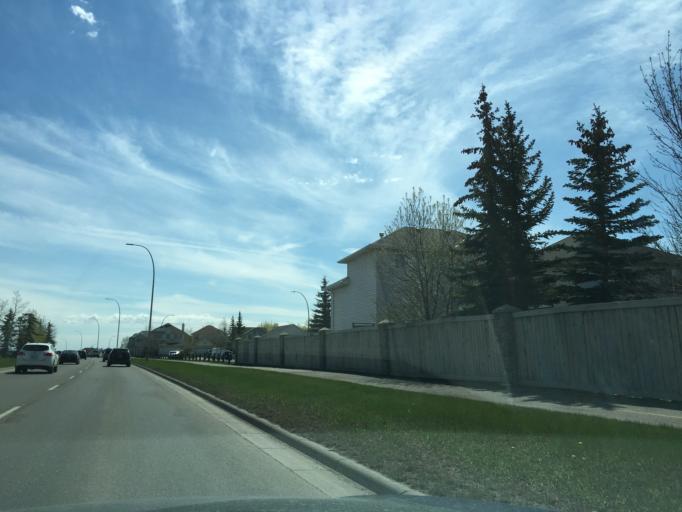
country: CA
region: Alberta
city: Calgary
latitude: 50.9032
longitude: -114.0869
